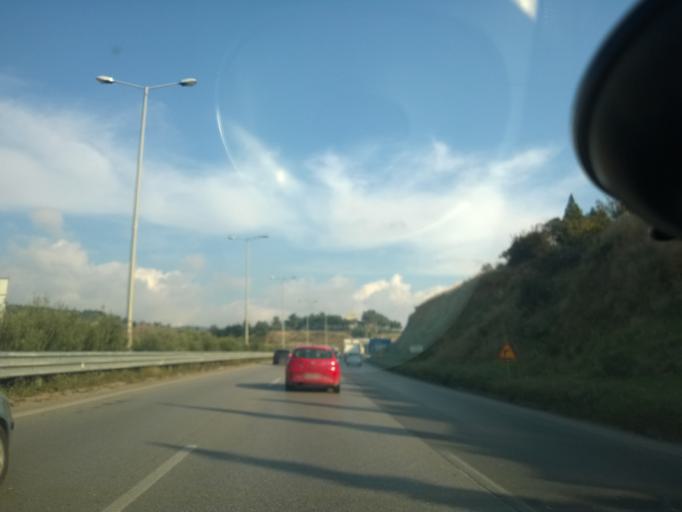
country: GR
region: Central Macedonia
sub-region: Nomos Thessalonikis
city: Pylaia
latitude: 40.6137
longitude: 22.9939
